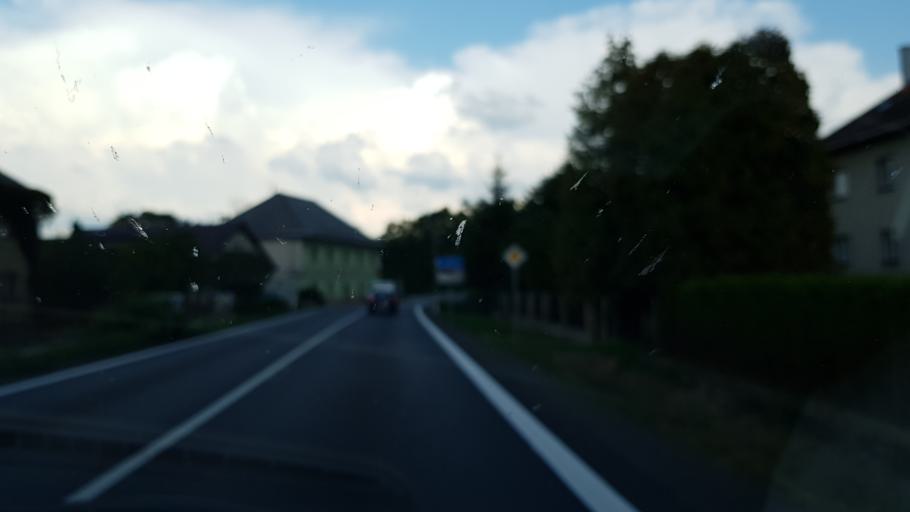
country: CZ
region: Pardubicky
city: Zamberk
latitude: 50.0941
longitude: 16.4432
